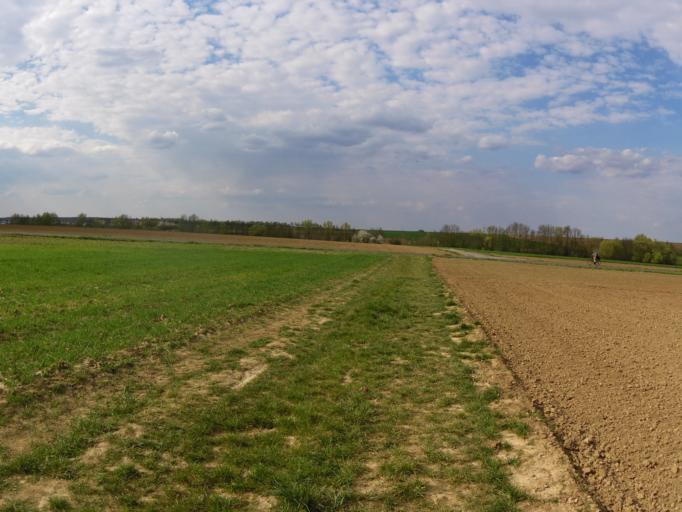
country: DE
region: Bavaria
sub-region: Regierungsbezirk Unterfranken
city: Kurnach
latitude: 49.8436
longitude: 10.0618
